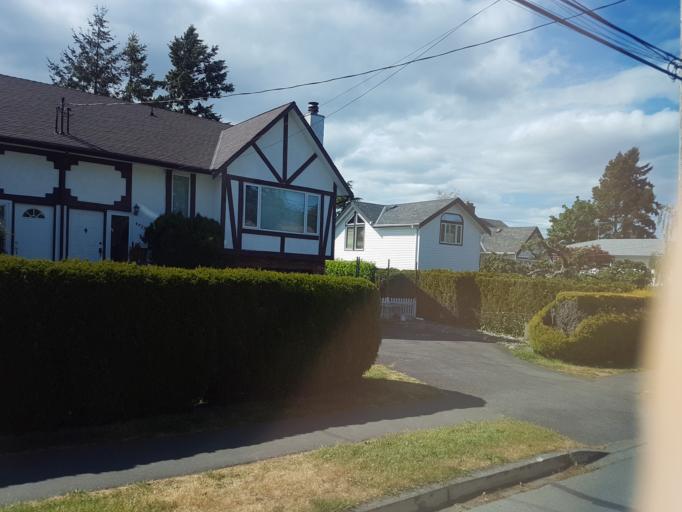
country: CA
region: British Columbia
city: Oak Bay
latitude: 48.4886
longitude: -123.3307
